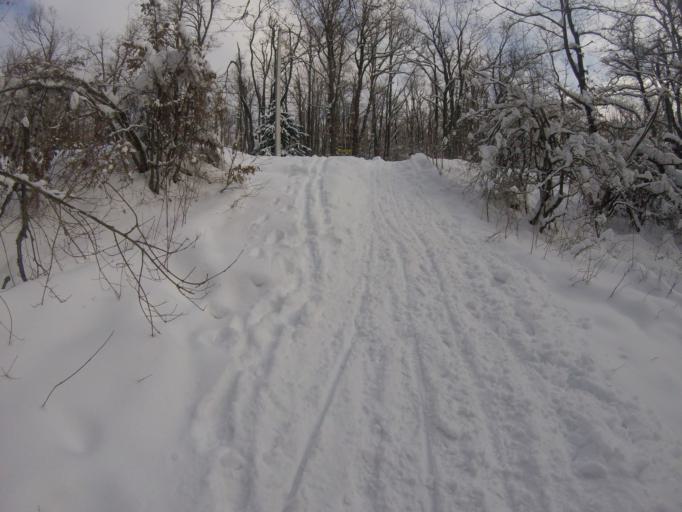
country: HU
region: Pest
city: Pilisszentkereszt
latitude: 47.7143
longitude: 18.8947
